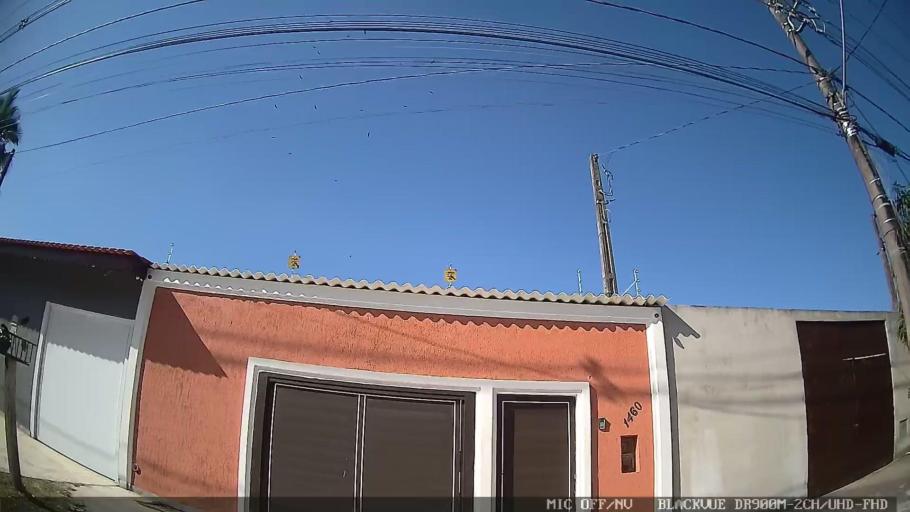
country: BR
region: Sao Paulo
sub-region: Guaruja
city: Guaruja
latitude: -23.9724
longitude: -46.2128
